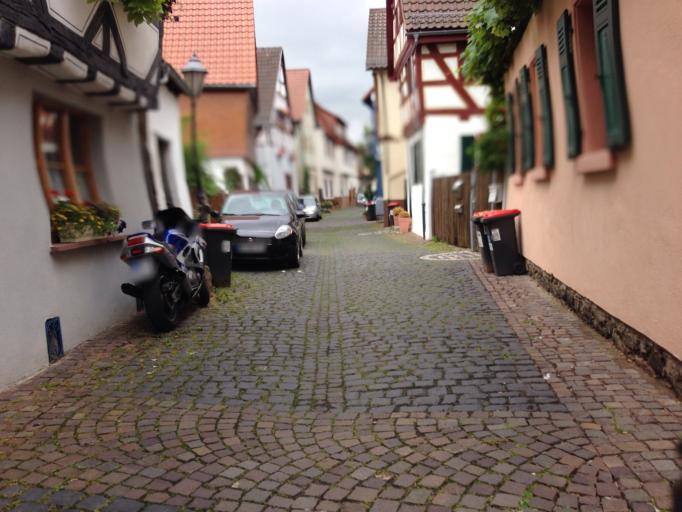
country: DE
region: Hesse
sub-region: Regierungsbezirk Darmstadt
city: Hanau am Main
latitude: 50.1073
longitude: 8.9147
